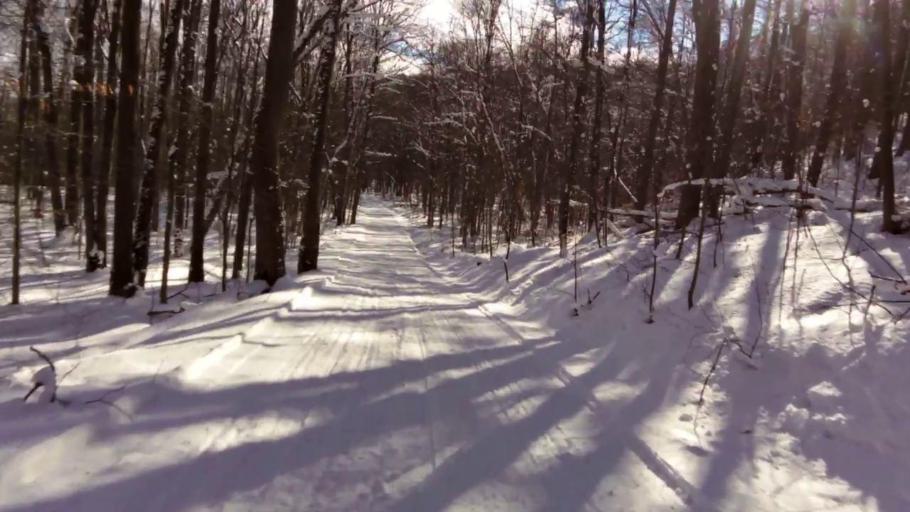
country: US
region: Pennsylvania
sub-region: McKean County
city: Foster Brook
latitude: 42.0671
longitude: -78.6622
